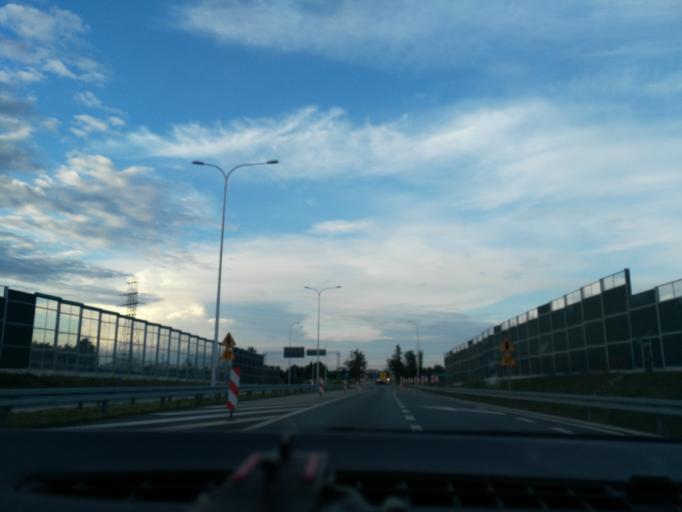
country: PL
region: Lublin Voivodeship
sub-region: Powiat lubelski
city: Jakubowice Murowane
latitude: 51.3083
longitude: 22.5952
